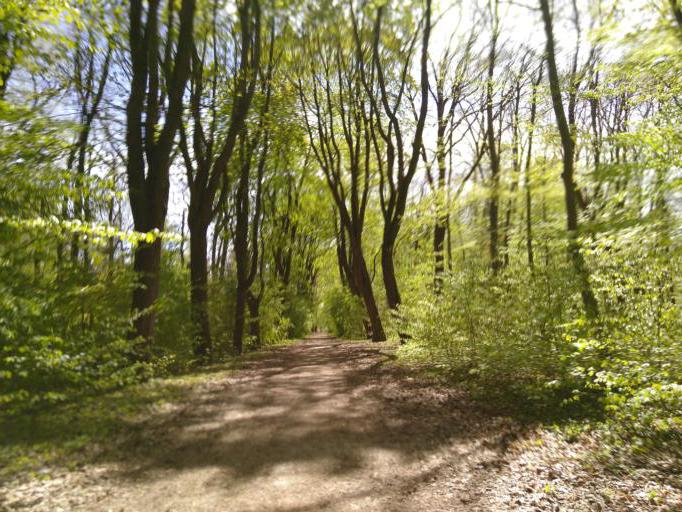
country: DE
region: Bavaria
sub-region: Upper Bavaria
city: Unterhaching
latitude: 48.0914
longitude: 11.6034
